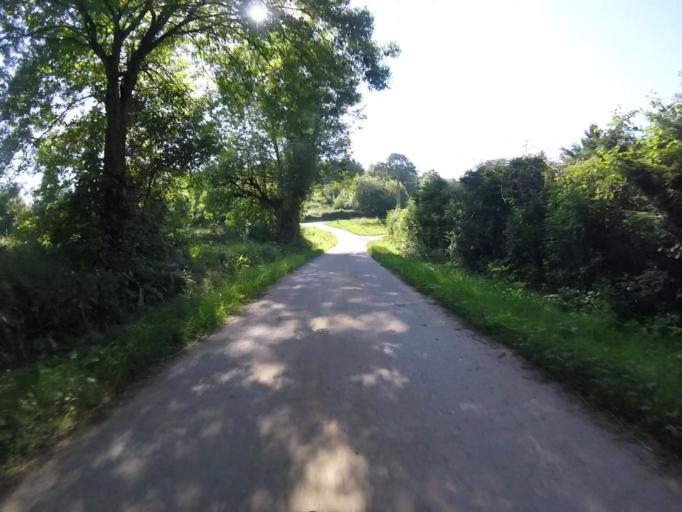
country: ES
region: Basque Country
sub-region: Provincia de Guipuzcoa
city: Astigarraga
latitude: 43.2729
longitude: -1.9268
